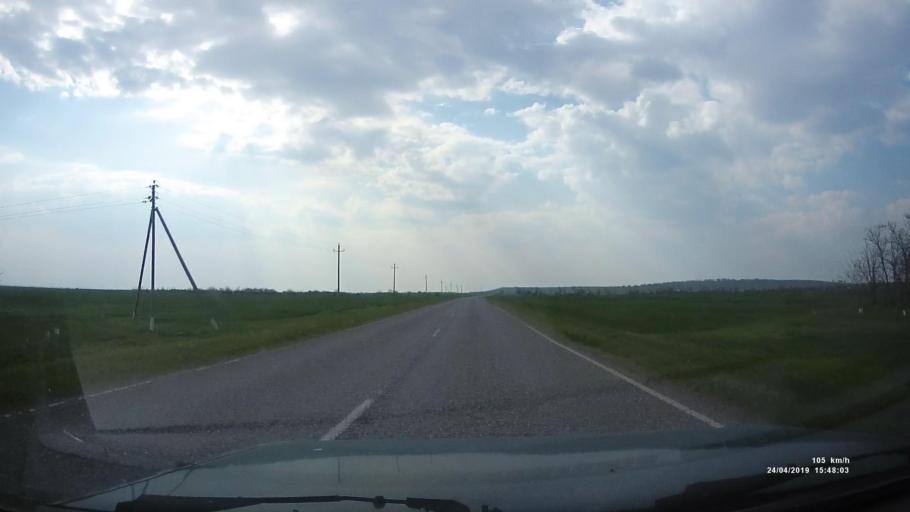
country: RU
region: Kalmykiya
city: Yashalta
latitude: 46.5967
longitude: 42.6840
